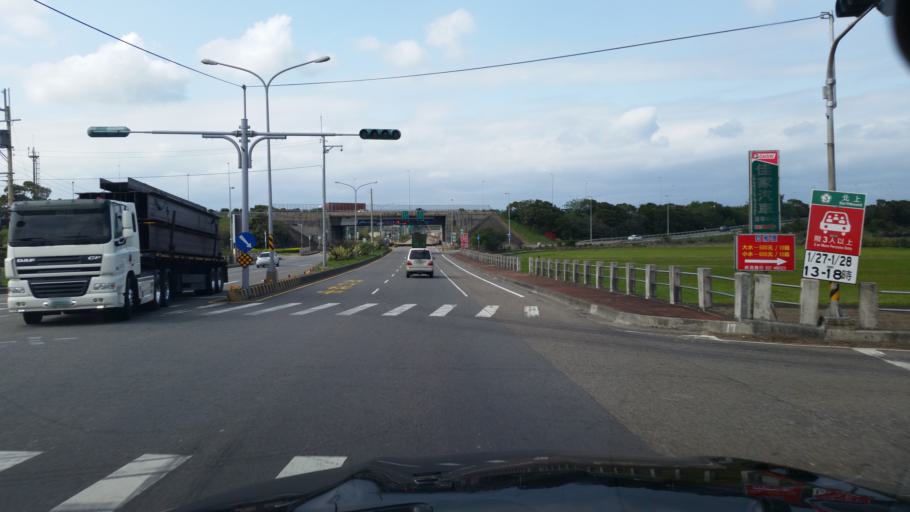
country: TW
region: Taiwan
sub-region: Miaoli
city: Miaoli
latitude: 24.6748
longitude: 120.8492
